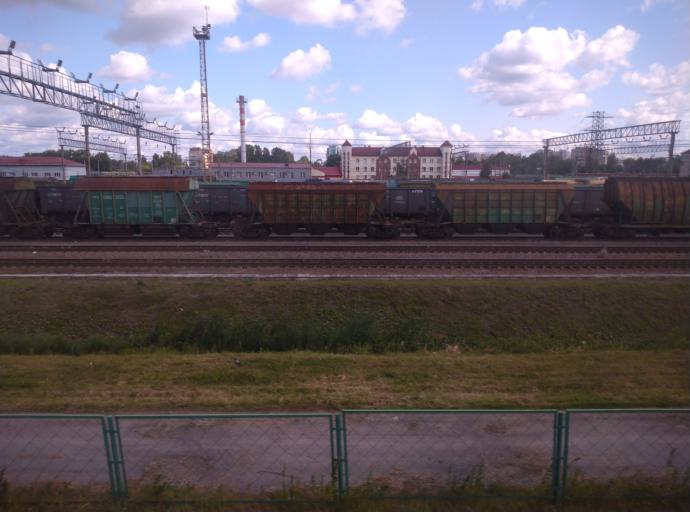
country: RU
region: St.-Petersburg
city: Obukhovo
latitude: 59.8636
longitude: 30.4305
